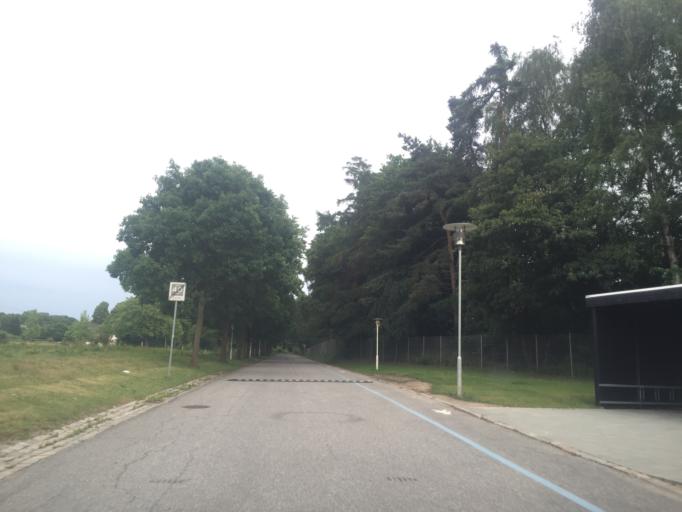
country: DK
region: Capital Region
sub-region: Lyngby-Tarbaek Kommune
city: Kongens Lyngby
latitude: 55.7792
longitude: 12.5350
